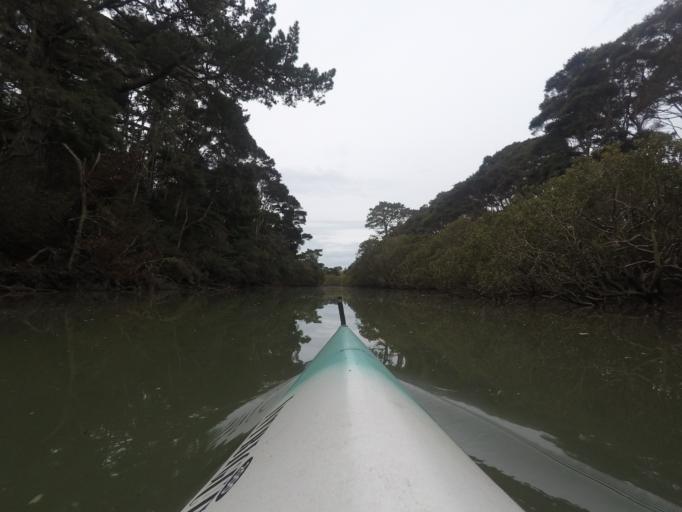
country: NZ
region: Auckland
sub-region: Auckland
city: Rothesay Bay
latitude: -36.6809
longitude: 174.7041
